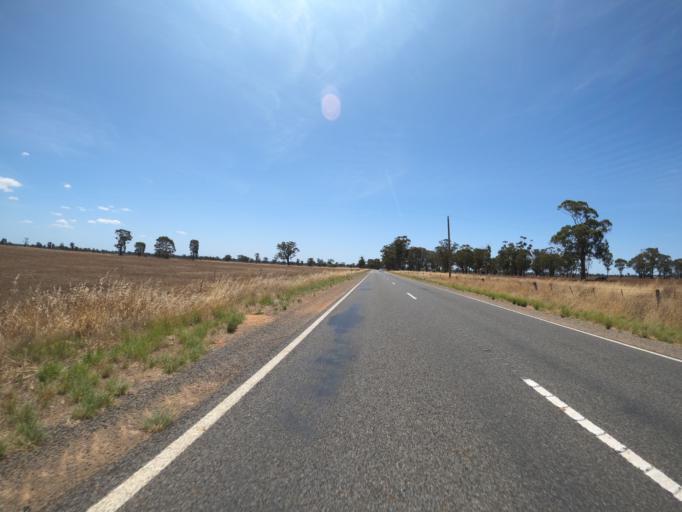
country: AU
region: Victoria
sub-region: Moira
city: Yarrawonga
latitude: -36.2007
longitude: 145.9672
